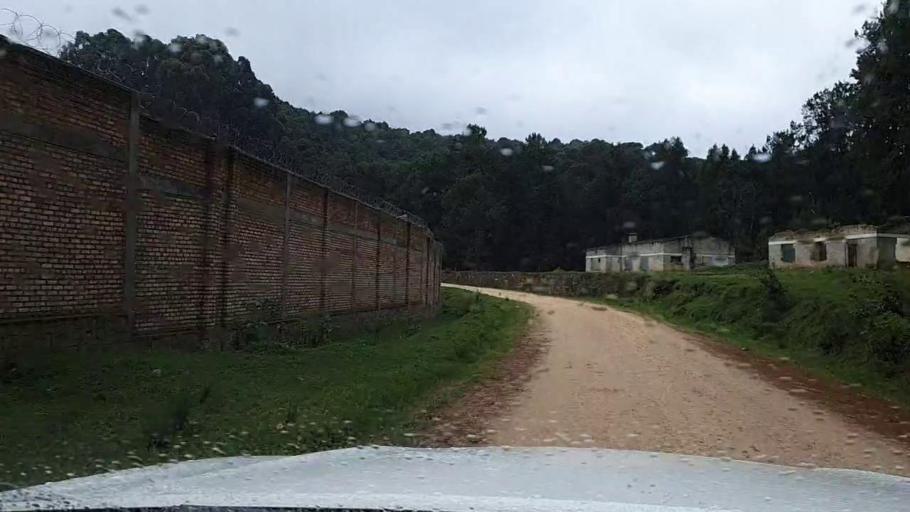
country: RW
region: Southern Province
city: Nzega
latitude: -2.3671
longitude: 29.3789
